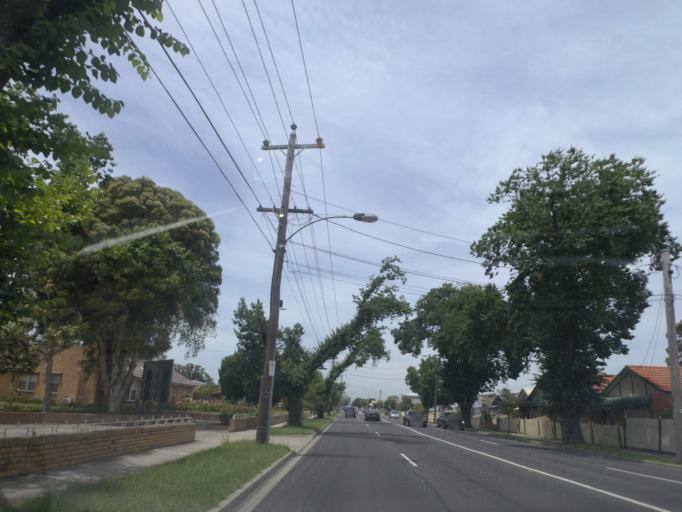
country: AU
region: Victoria
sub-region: Maribyrnong
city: Maribyrnong
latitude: -37.7876
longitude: 144.8808
